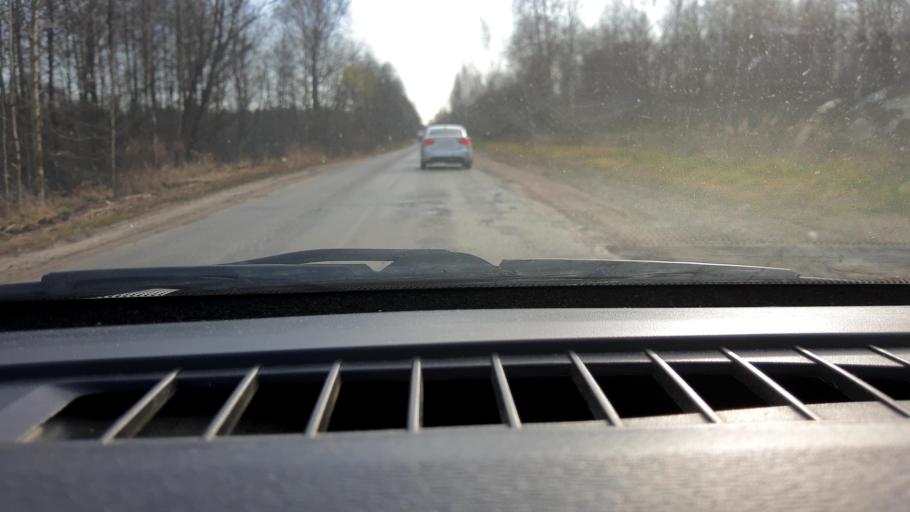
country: RU
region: Nizjnij Novgorod
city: Neklyudovo
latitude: 56.4346
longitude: 43.9217
